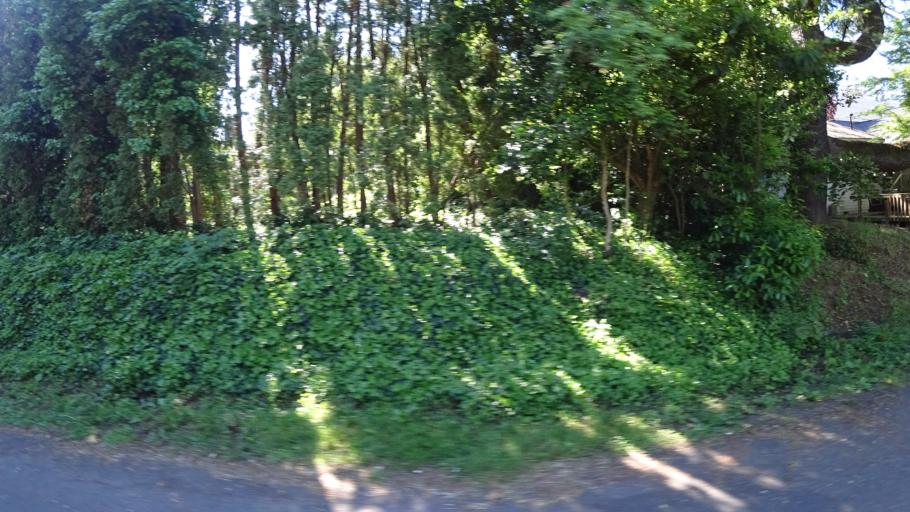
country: US
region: Oregon
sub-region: Washington County
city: Raleigh Hills
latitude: 45.4839
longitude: -122.7198
